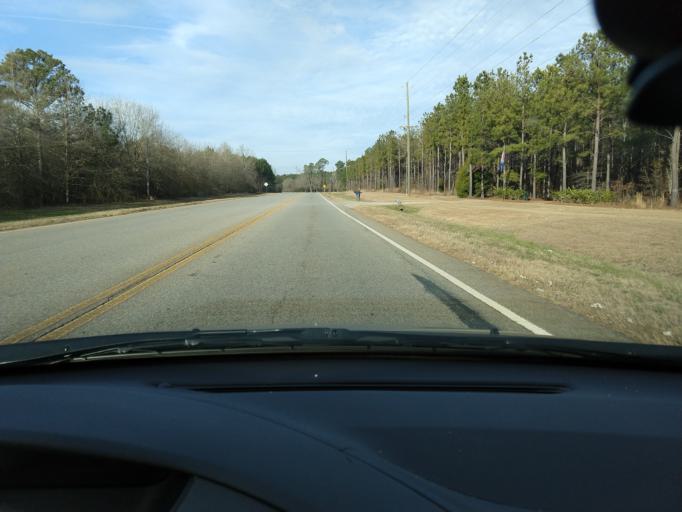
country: US
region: Georgia
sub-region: Sumter County
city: Americus
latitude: 32.0557
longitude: -84.3155
